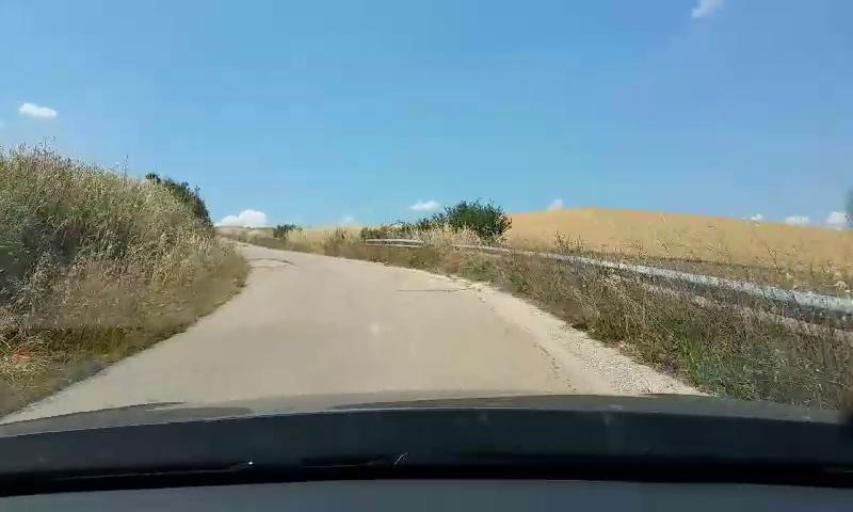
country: IT
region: Molise
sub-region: Provincia di Campobasso
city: Montecilfone
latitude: 41.9220
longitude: 14.8454
